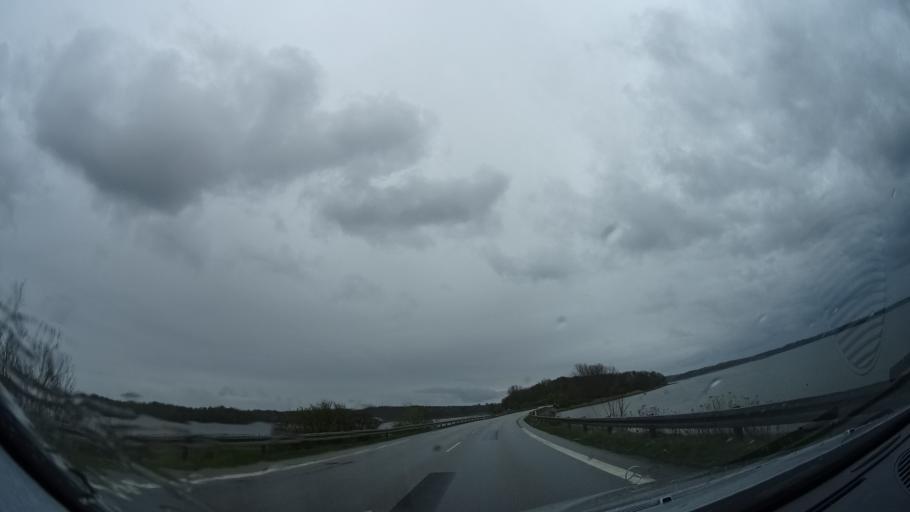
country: DK
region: Zealand
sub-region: Lejre Kommune
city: Ejby
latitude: 55.6803
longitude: 11.8039
